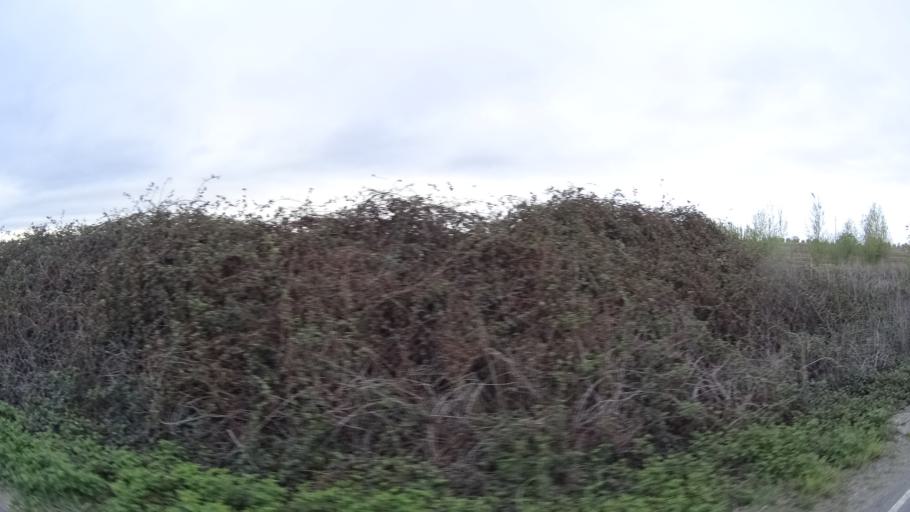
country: US
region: California
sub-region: Glenn County
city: Willows
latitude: 39.4063
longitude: -122.1222
